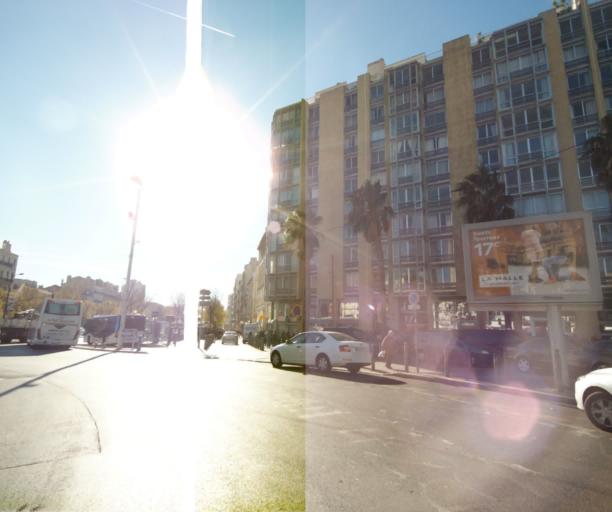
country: FR
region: Provence-Alpes-Cote d'Azur
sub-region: Departement des Bouches-du-Rhone
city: Marseille 06
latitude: 43.2858
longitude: 5.3835
